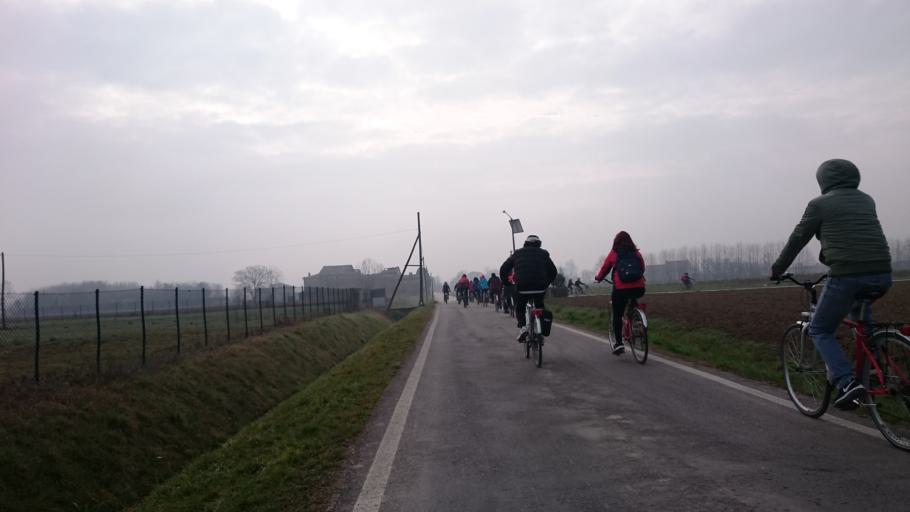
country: IT
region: Veneto
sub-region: Provincia di Vicenza
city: Montegalda
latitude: 45.4719
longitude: 11.6468
